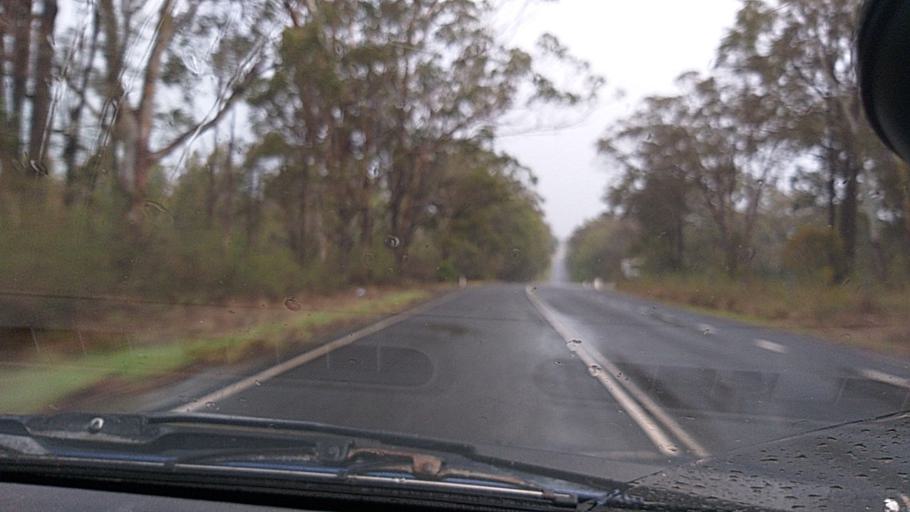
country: AU
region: New South Wales
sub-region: Wollondilly
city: Douglas Park
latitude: -34.2162
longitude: 150.7229
